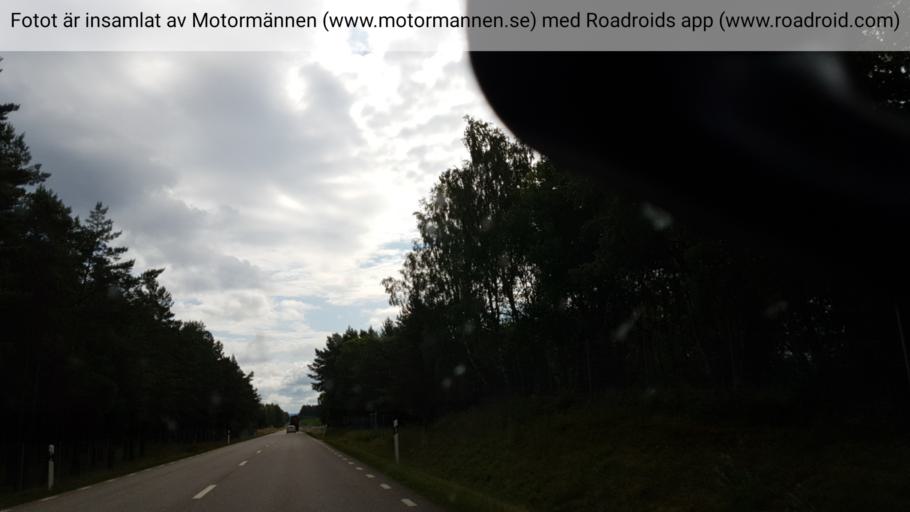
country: SE
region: Vaestra Goetaland
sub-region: Vara Kommun
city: Kvanum
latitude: 58.2123
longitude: 13.2482
